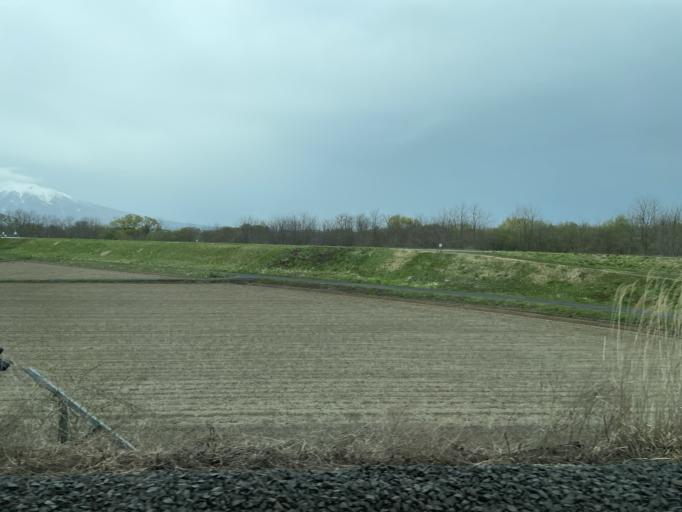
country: JP
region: Aomori
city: Hirosaki
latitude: 40.6419
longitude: 140.5168
